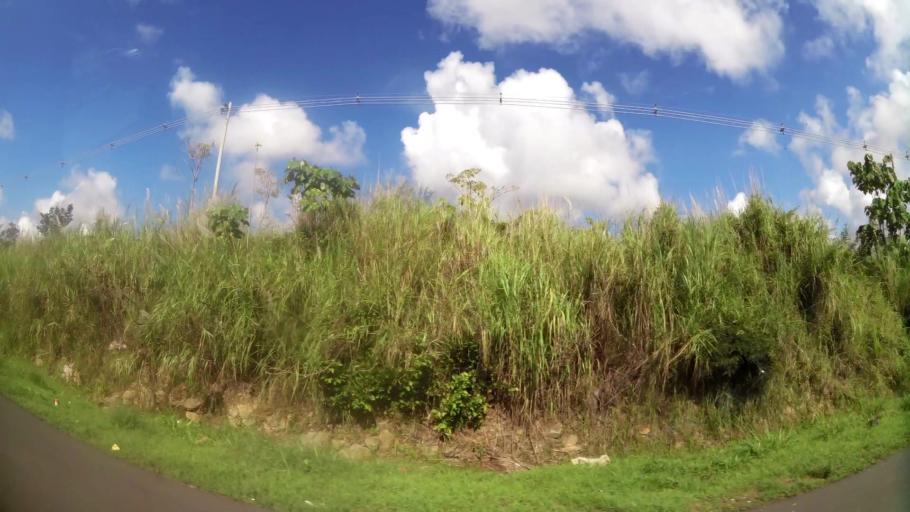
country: PA
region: Panama
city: Nuevo Arraijan
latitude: 8.9007
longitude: -79.7412
